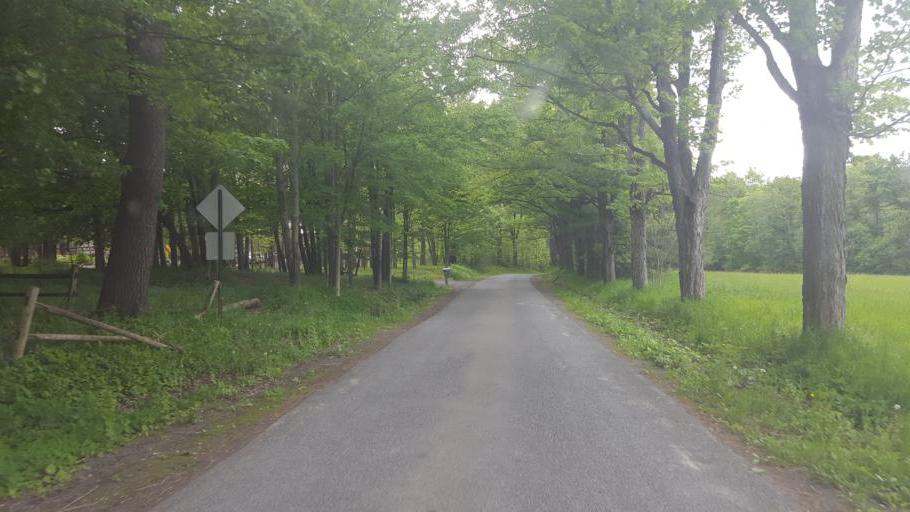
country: US
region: New York
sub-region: Otsego County
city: Richfield Springs
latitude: 42.8602
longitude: -74.9722
